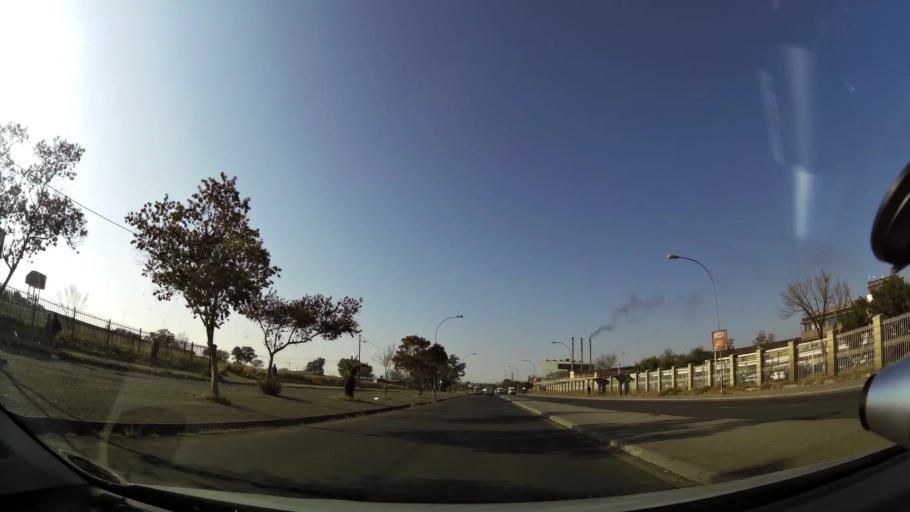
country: ZA
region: Orange Free State
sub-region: Mangaung Metropolitan Municipality
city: Bloemfontein
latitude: -29.1390
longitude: 26.2450
